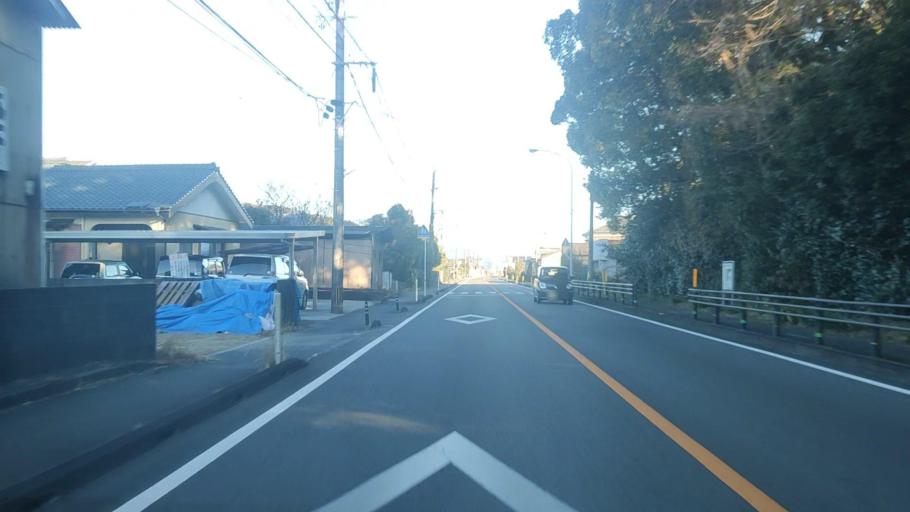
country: JP
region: Miyazaki
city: Nobeoka
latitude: 32.3819
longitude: 131.6276
